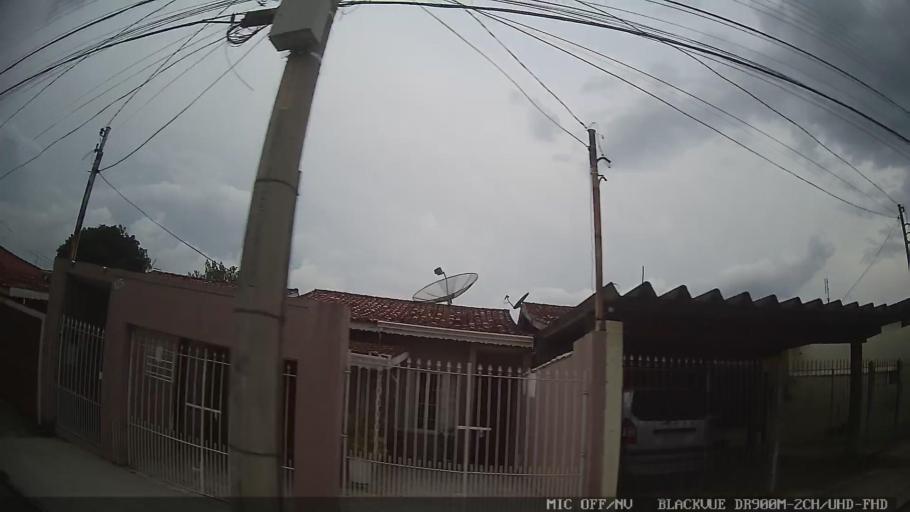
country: BR
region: Sao Paulo
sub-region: Atibaia
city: Atibaia
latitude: -23.1253
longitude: -46.5591
